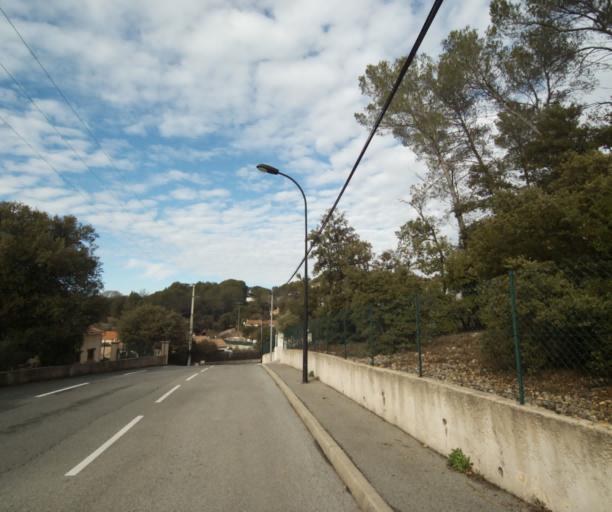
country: FR
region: Provence-Alpes-Cote d'Azur
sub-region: Departement du Var
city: Trans-en-Provence
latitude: 43.5025
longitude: 6.4950
